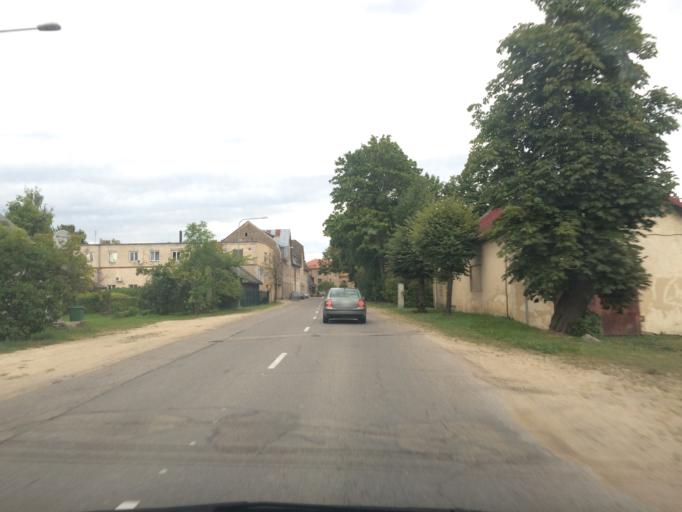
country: LV
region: Plavinu
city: Plavinas
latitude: 56.6151
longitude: 25.7191
